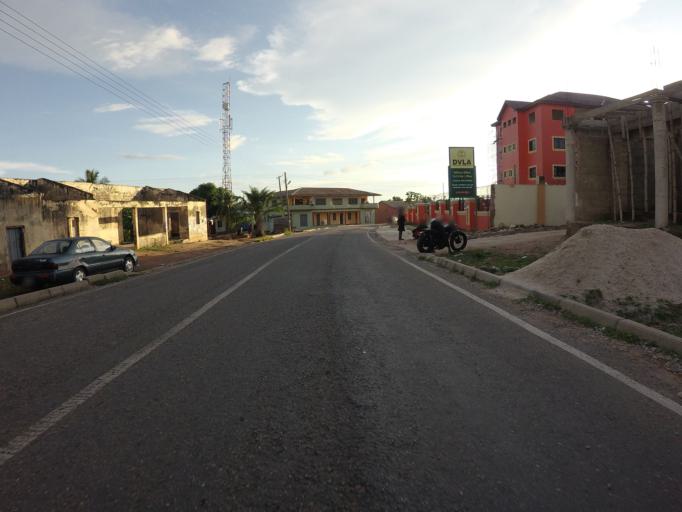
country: GH
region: Ashanti
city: Tafo
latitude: 6.9395
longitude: -1.6766
